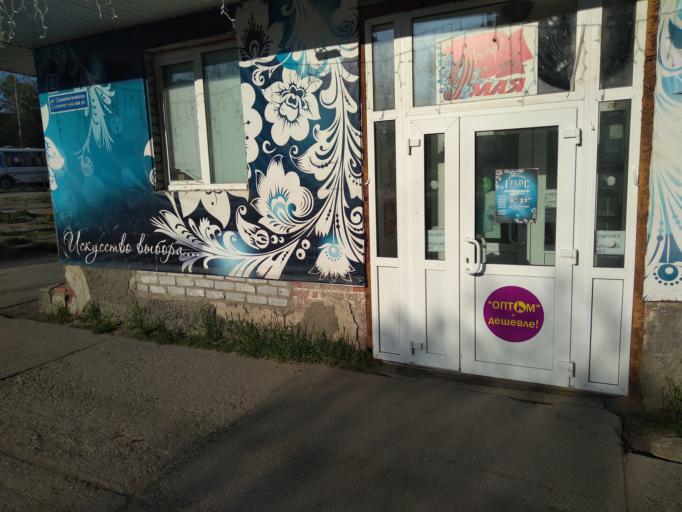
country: RU
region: Komi Republic
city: Pechora
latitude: 65.1089
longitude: 57.1545
